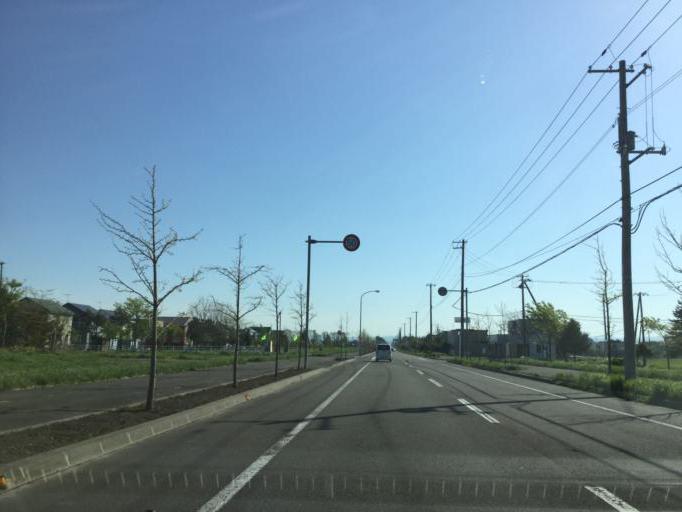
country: JP
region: Hokkaido
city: Ebetsu
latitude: 43.0610
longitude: 141.6606
